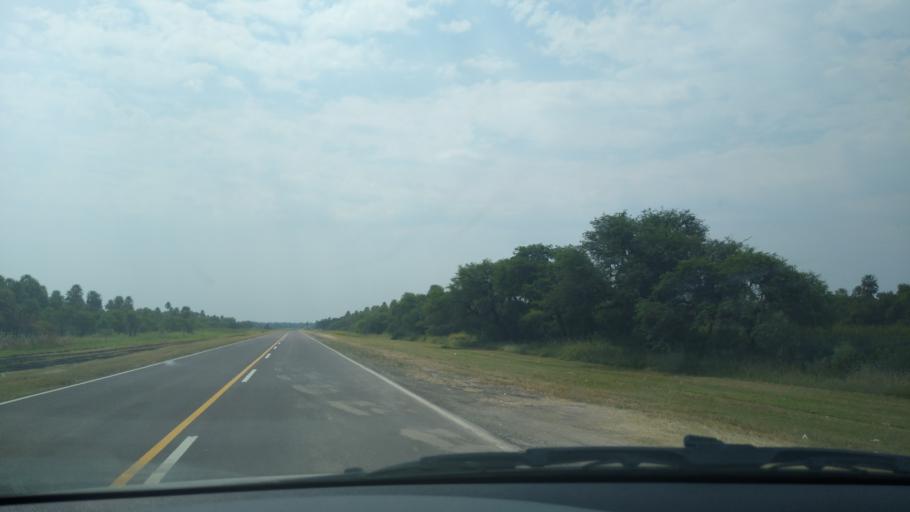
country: AR
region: Chaco
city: Margarita Belen
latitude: -27.0825
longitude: -58.9598
